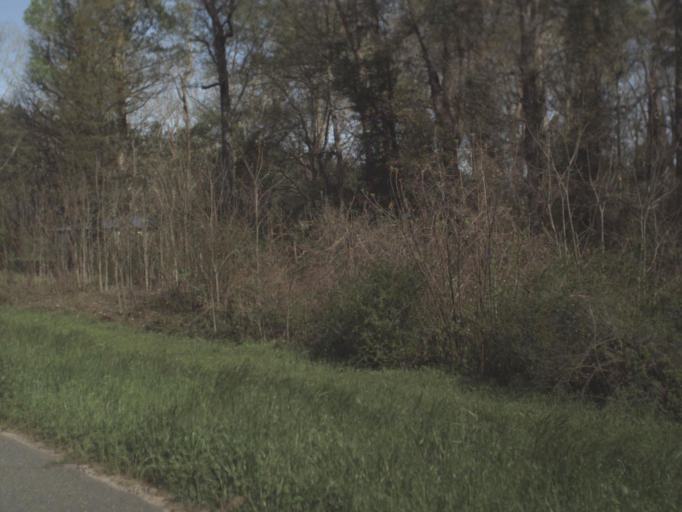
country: US
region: Alabama
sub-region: Houston County
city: Cottonwood
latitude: 30.9456
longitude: -85.3522
